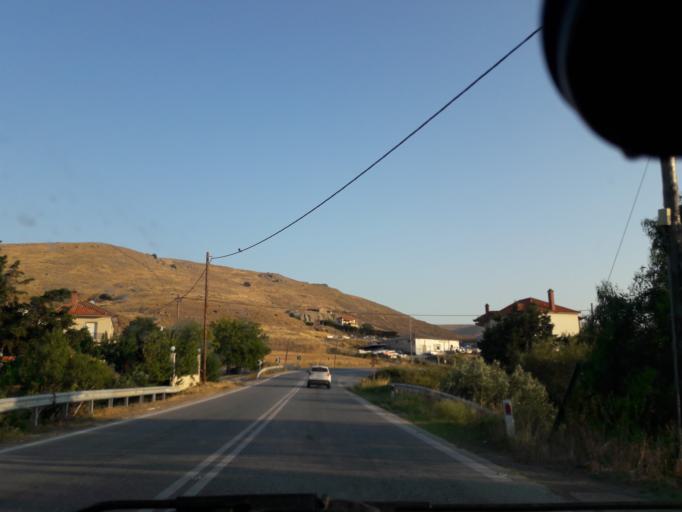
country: GR
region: North Aegean
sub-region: Nomos Lesvou
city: Myrina
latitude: 39.9064
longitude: 25.1122
